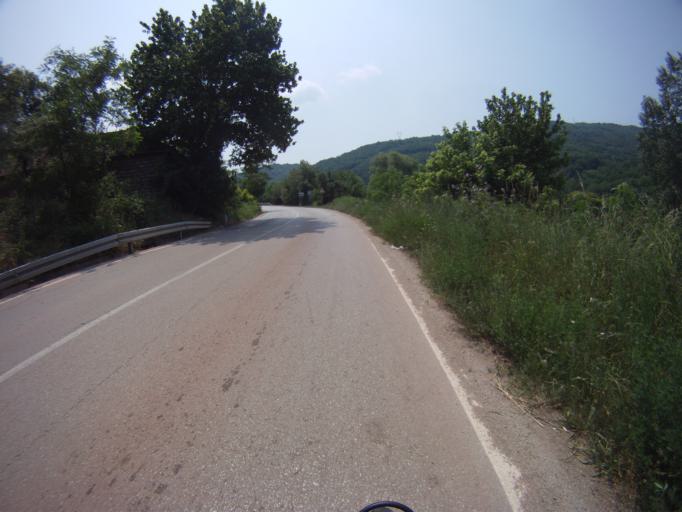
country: RS
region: Central Serbia
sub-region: Nisavski Okrug
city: Gadzin Han
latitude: 43.2412
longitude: 22.0154
